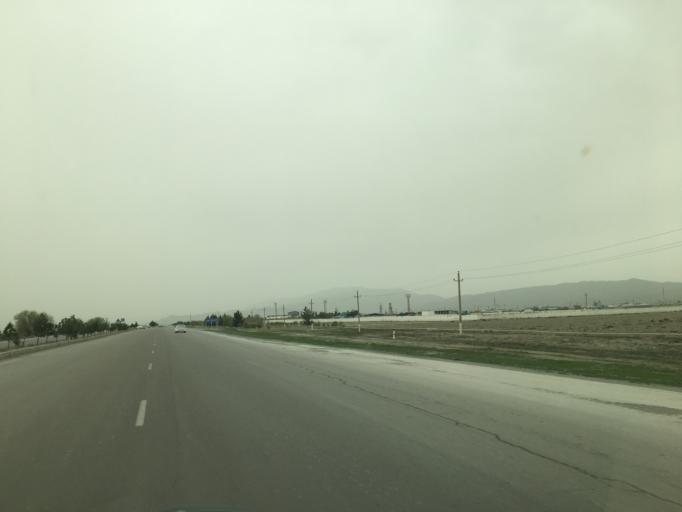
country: TM
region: Ahal
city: Baharly
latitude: 38.3266
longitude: 57.5865
